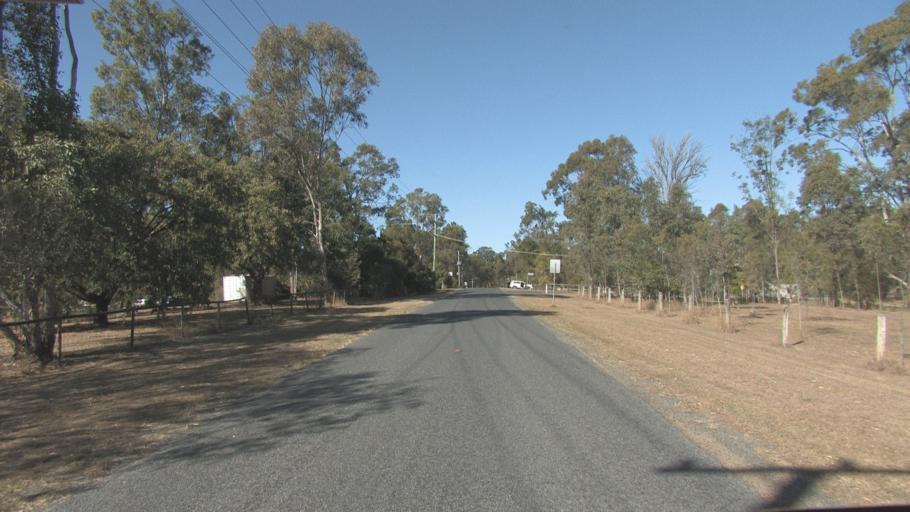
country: AU
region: Queensland
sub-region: Logan
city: Cedar Vale
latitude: -27.8730
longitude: 152.9841
